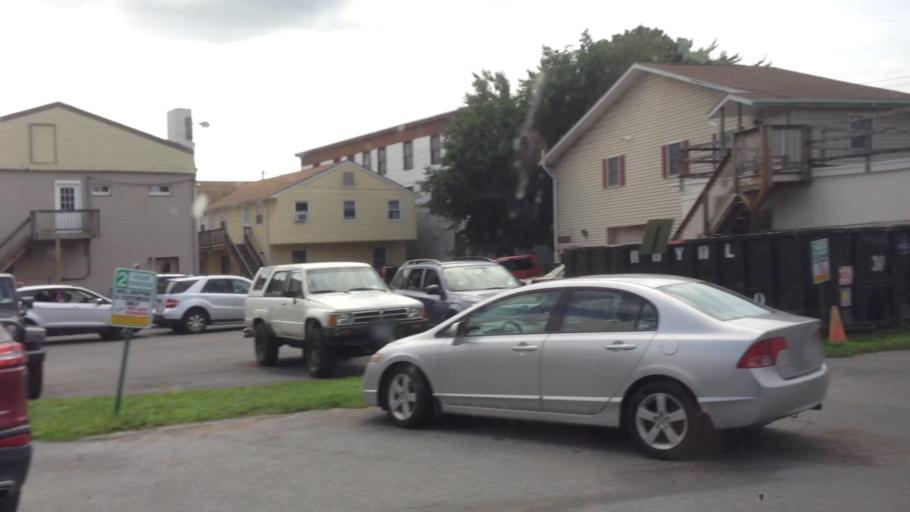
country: US
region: New York
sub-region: Dutchess County
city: Red Hook
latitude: 41.9955
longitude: -73.8744
